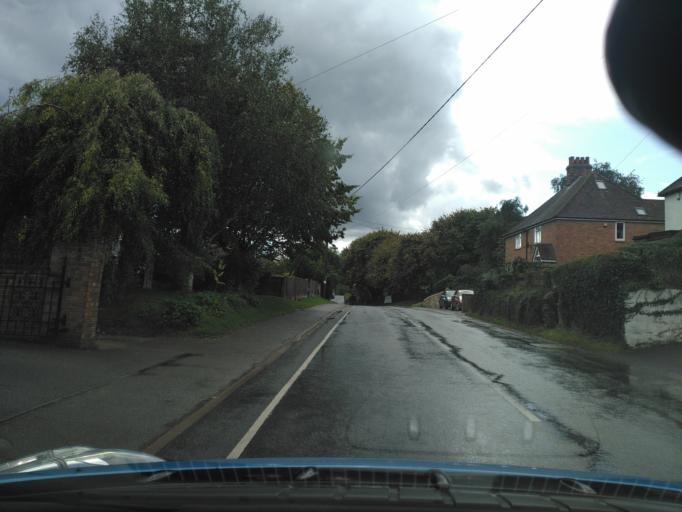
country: GB
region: England
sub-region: Oxfordshire
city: Wheatley
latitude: 51.7185
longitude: -1.1592
